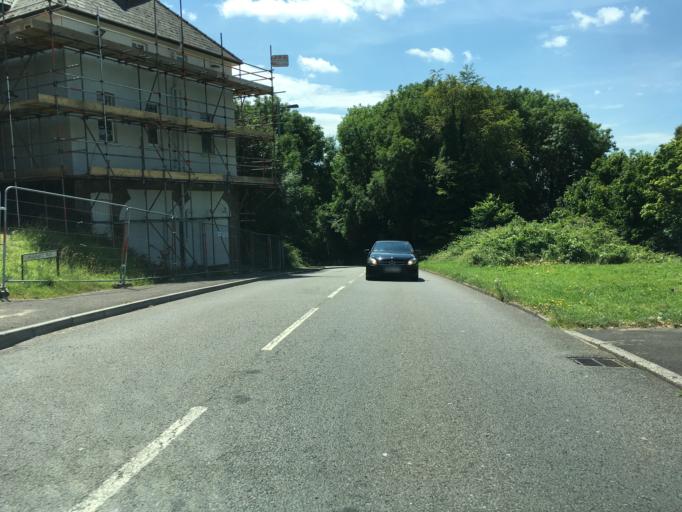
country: GB
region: Wales
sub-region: Newport
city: Newport
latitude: 51.5764
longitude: -3.0192
